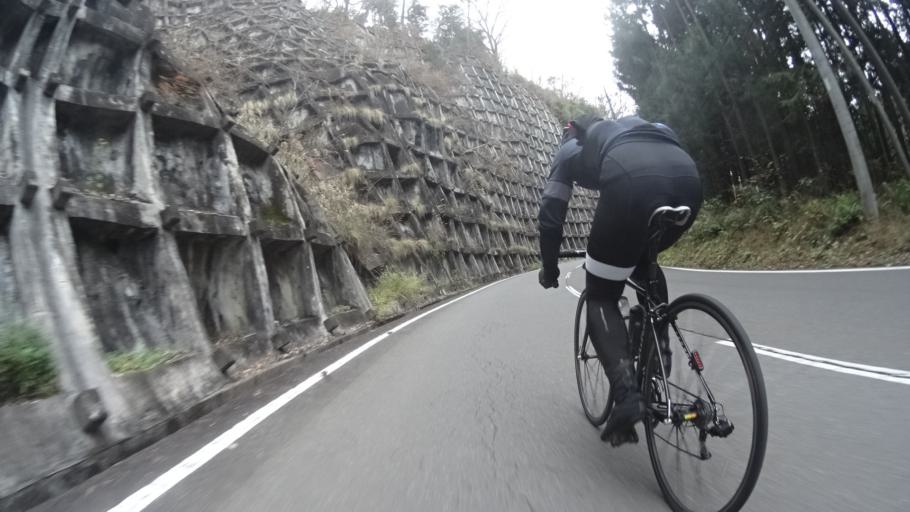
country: JP
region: Yamanashi
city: Uenohara
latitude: 35.6385
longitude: 139.0726
